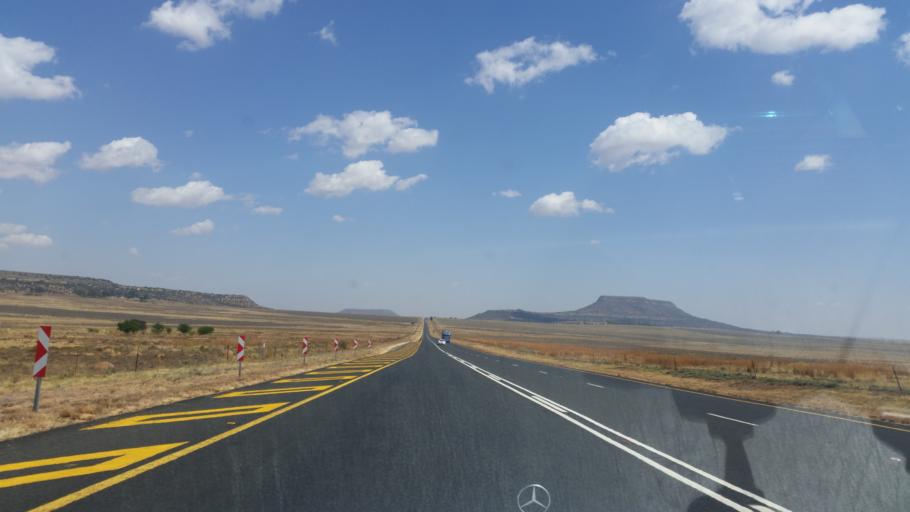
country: ZA
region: Orange Free State
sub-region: Thabo Mofutsanyana District Municipality
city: Senekal
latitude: -28.3087
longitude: 27.8284
